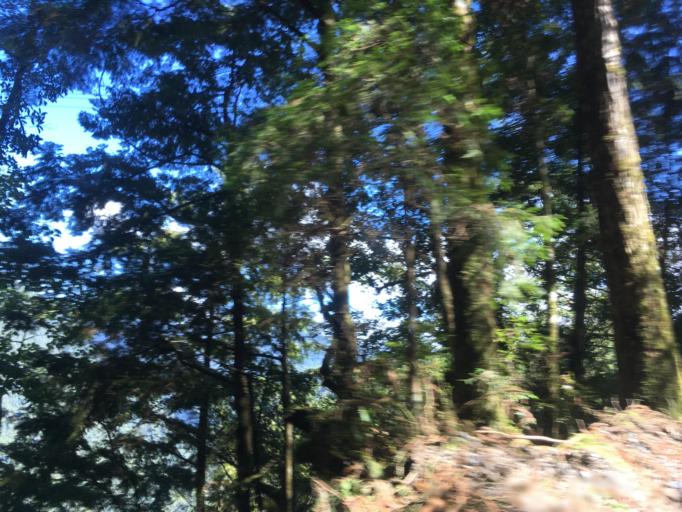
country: TW
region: Taiwan
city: Daxi
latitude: 24.5986
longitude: 121.4457
